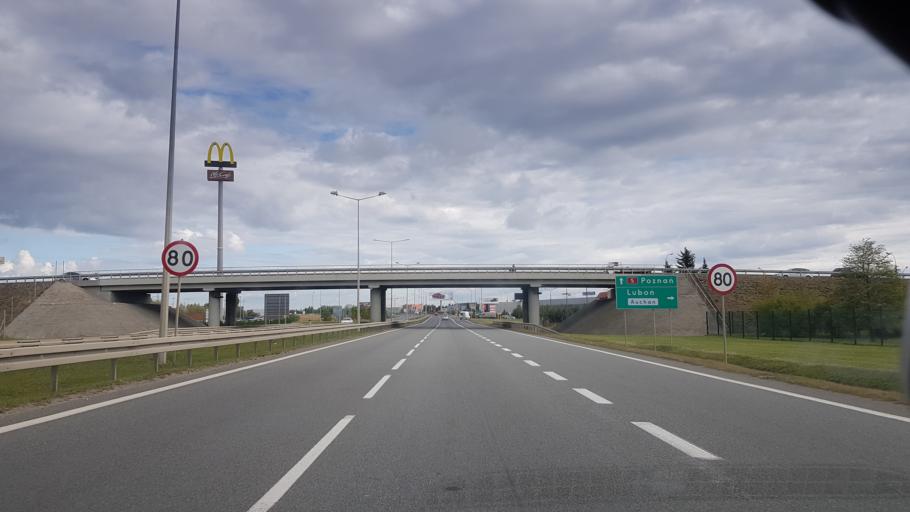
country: PL
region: Greater Poland Voivodeship
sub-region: Powiat poznanski
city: Komorniki
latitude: 52.3527
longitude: 16.8416
